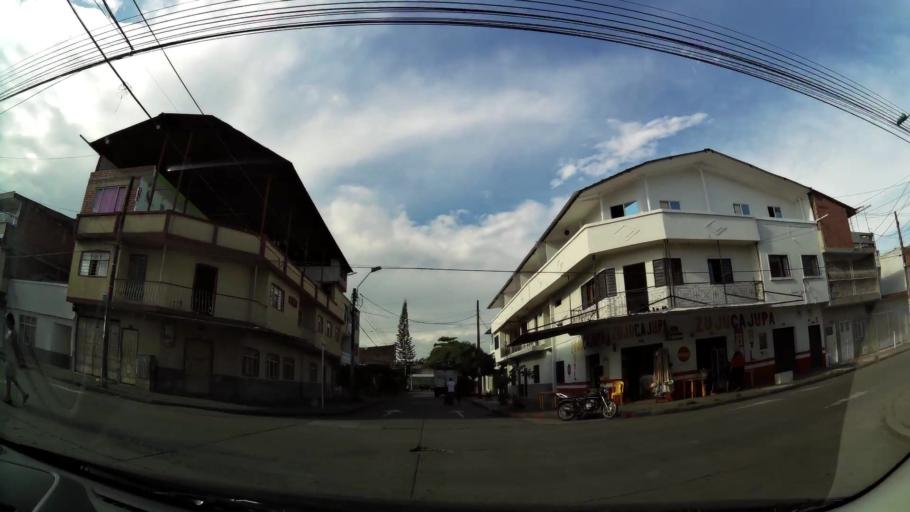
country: CO
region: Valle del Cauca
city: Cali
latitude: 3.4224
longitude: -76.5250
